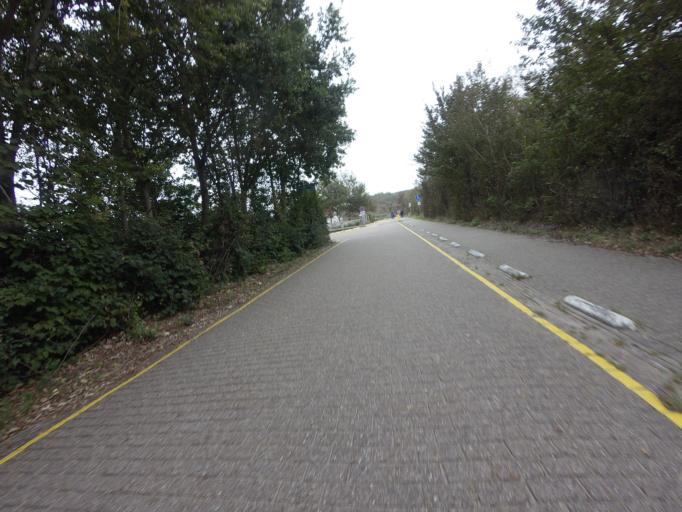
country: NL
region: Zeeland
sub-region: Gemeente Vlissingen
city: Vlissingen
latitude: 51.4955
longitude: 3.4996
